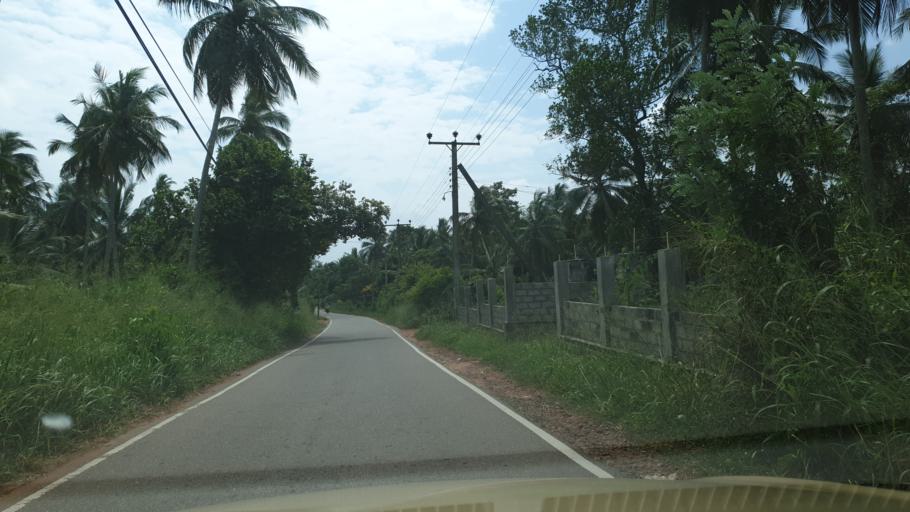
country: LK
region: North Western
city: Kuliyapitiya
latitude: 7.3512
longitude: 79.9783
